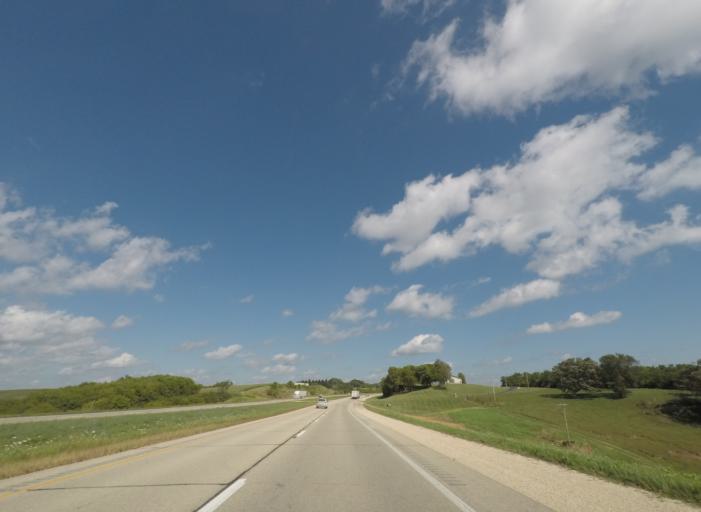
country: US
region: Iowa
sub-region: Dubuque County
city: Cascade
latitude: 42.3152
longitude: -90.9684
